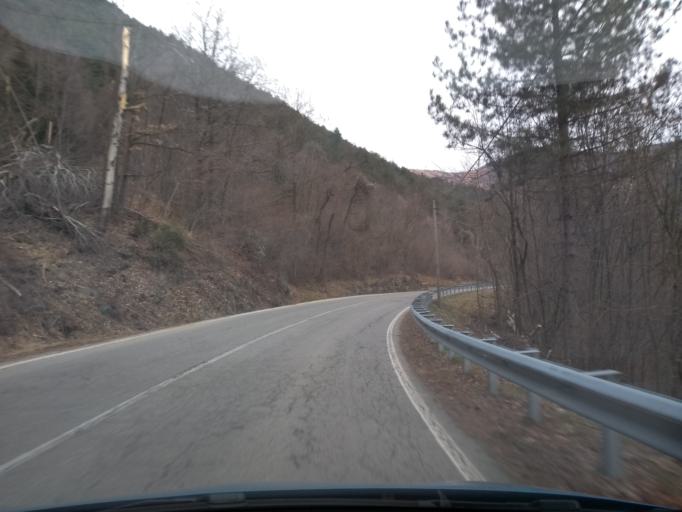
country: IT
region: Piedmont
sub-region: Provincia di Torino
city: La Villa
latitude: 45.2378
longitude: 7.4206
